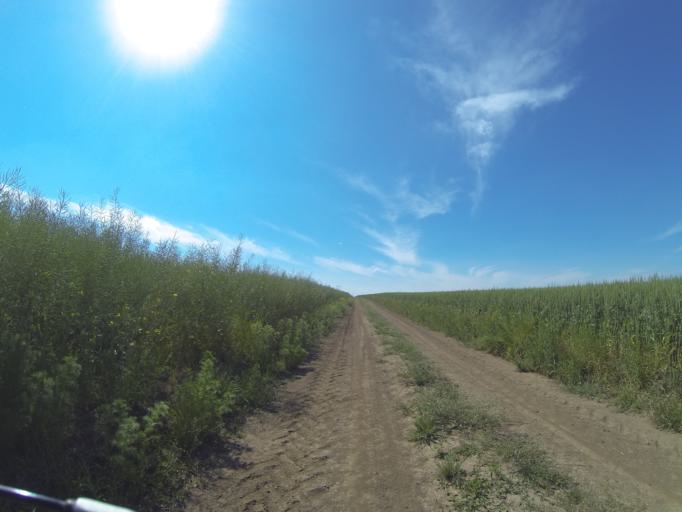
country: RO
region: Dolj
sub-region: Comuna Leu
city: Leu
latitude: 44.2558
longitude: 24.0095
